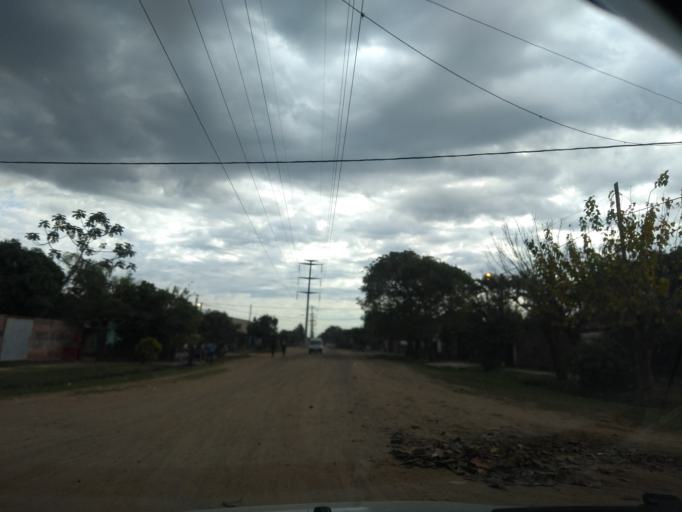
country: AR
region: Chaco
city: Barranqueras
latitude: -27.4736
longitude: -58.9181
